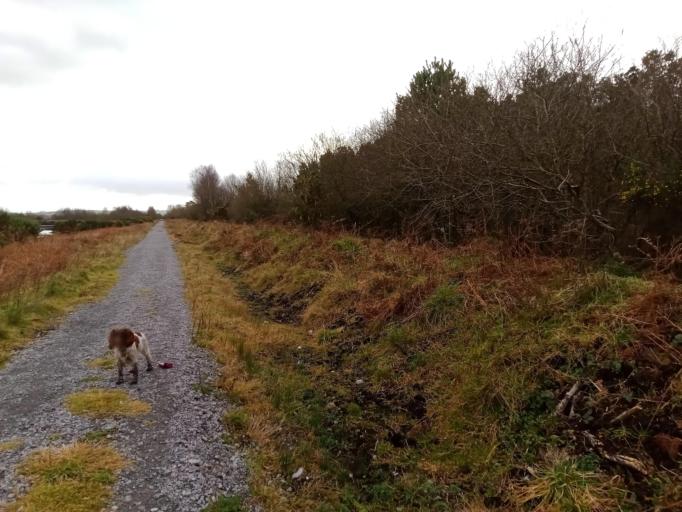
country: IE
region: Munster
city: Thurles
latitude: 52.5961
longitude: -7.7453
